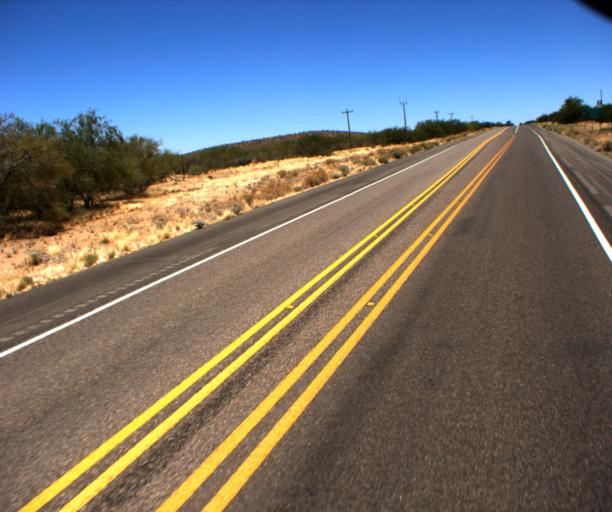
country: US
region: Arizona
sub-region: Pima County
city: Sells
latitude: 32.0148
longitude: -111.6386
